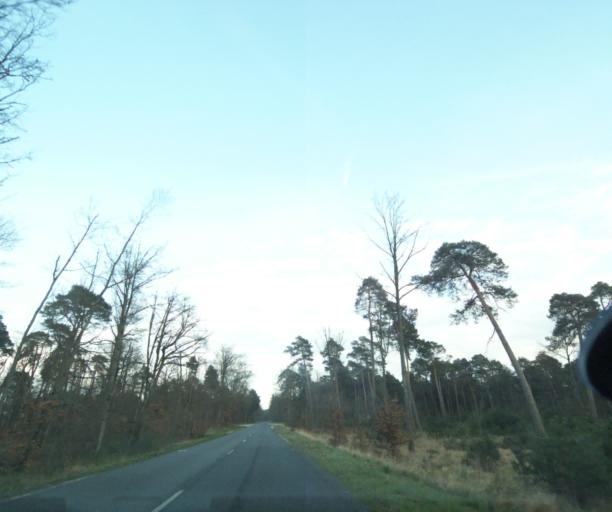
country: FR
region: Ile-de-France
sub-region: Departement de Seine-et-Marne
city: Avon
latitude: 48.3802
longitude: 2.7317
